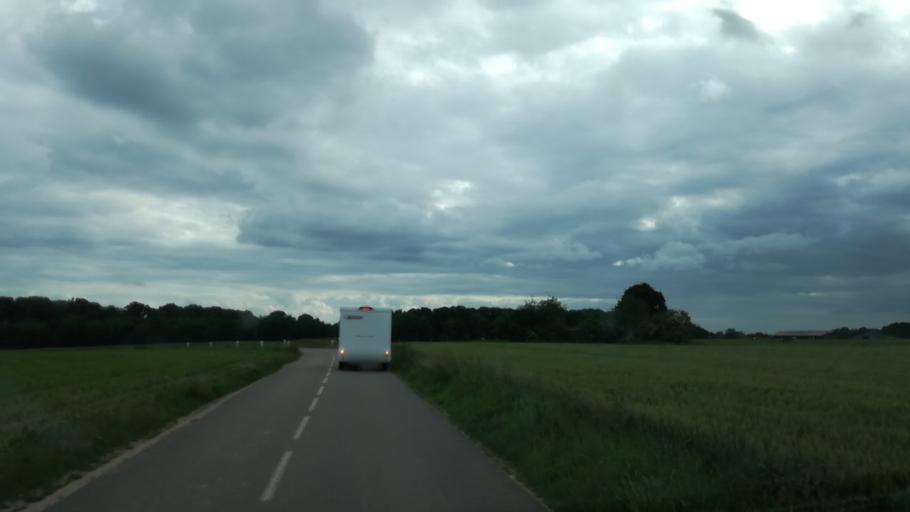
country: FR
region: Haute-Normandie
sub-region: Departement de l'Eure
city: Bourg-Achard
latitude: 49.3394
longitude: 0.8127
